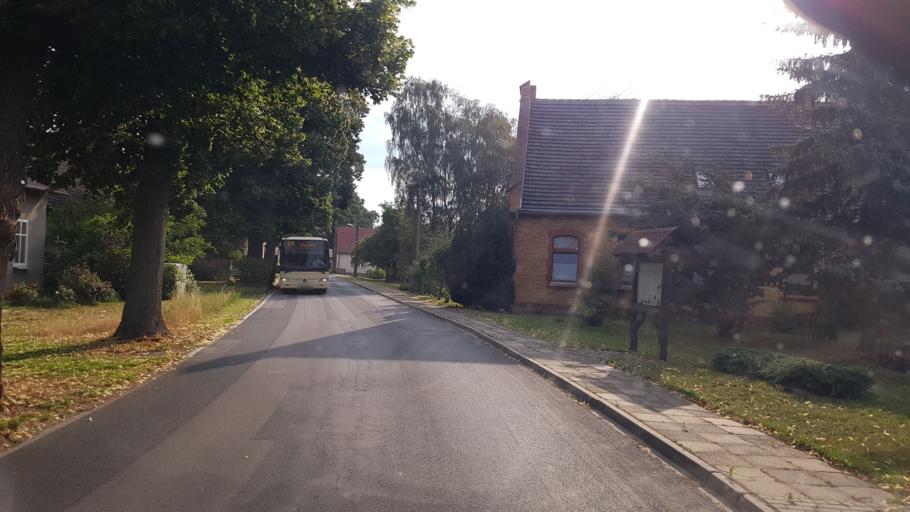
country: DE
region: Brandenburg
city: Golssen
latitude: 51.9704
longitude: 13.5673
